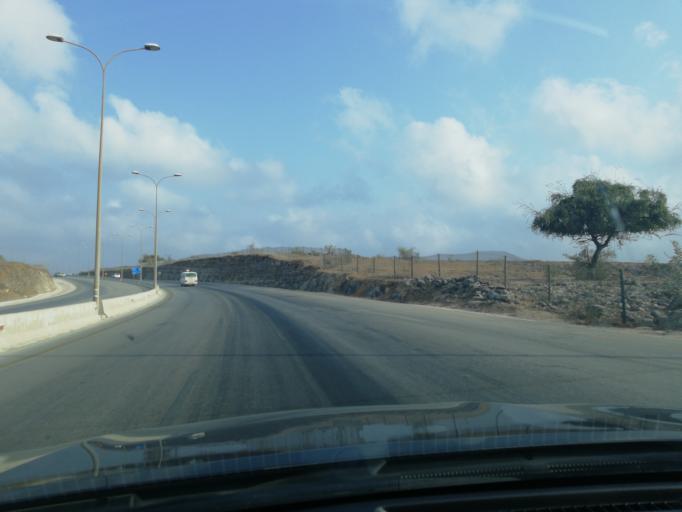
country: OM
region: Zufar
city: Salalah
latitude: 17.1929
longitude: 54.1140
